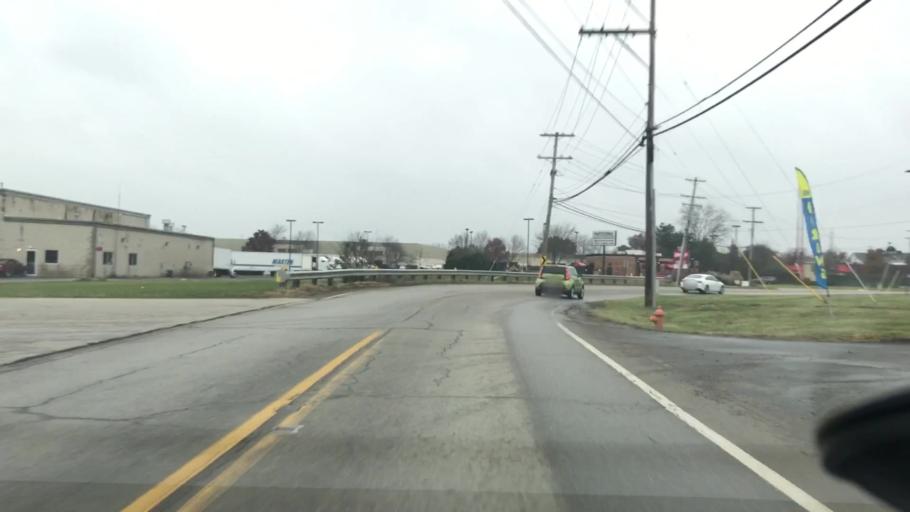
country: US
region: Ohio
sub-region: Franklin County
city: Upper Arlington
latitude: 40.0022
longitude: -83.1099
